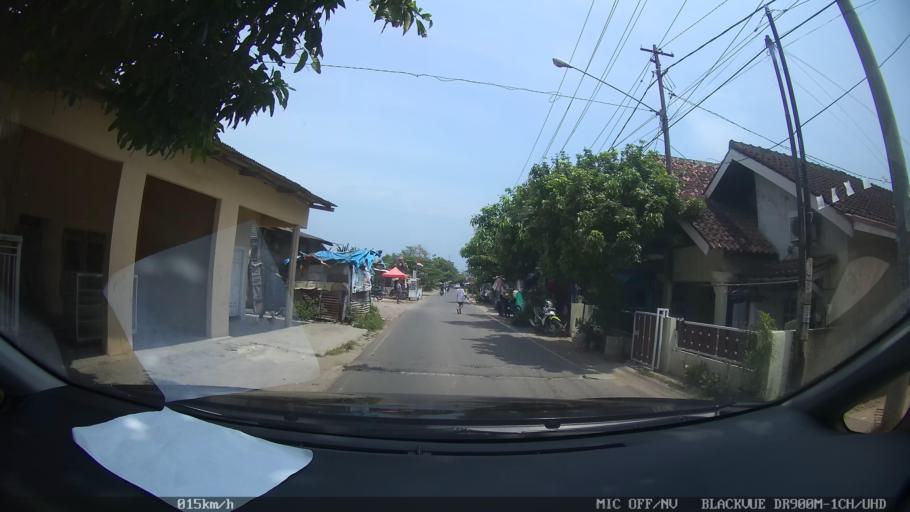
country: ID
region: Lampung
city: Bandarlampung
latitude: -5.4489
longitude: 105.2550
